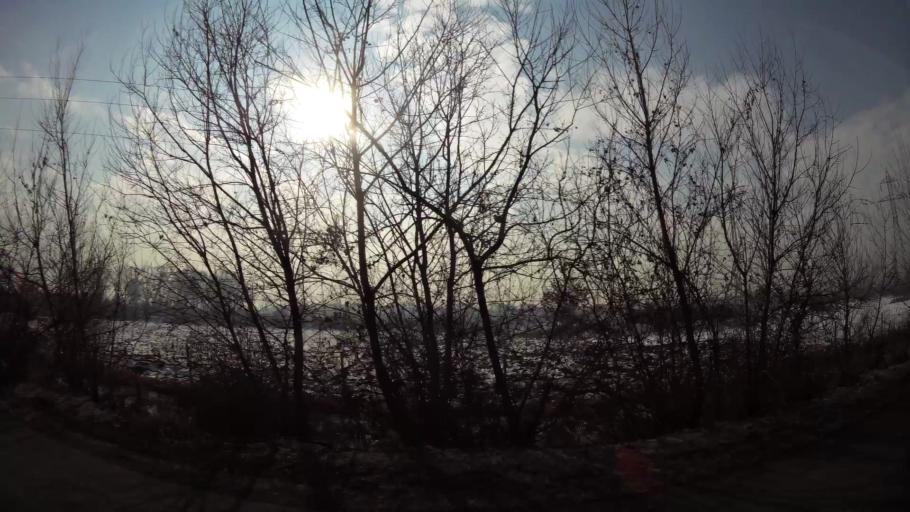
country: MK
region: Butel
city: Butel
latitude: 42.0380
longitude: 21.4651
